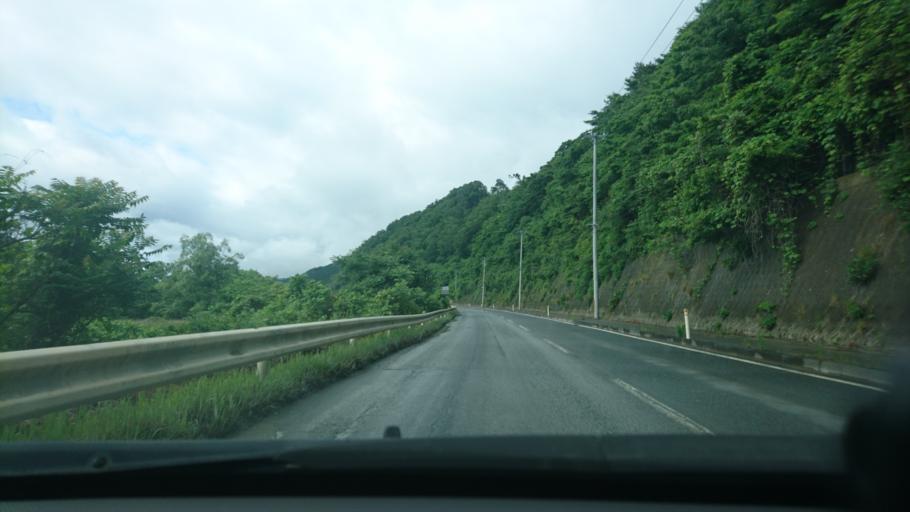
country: JP
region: Miyagi
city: Ishinomaki
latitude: 38.5822
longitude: 141.3036
